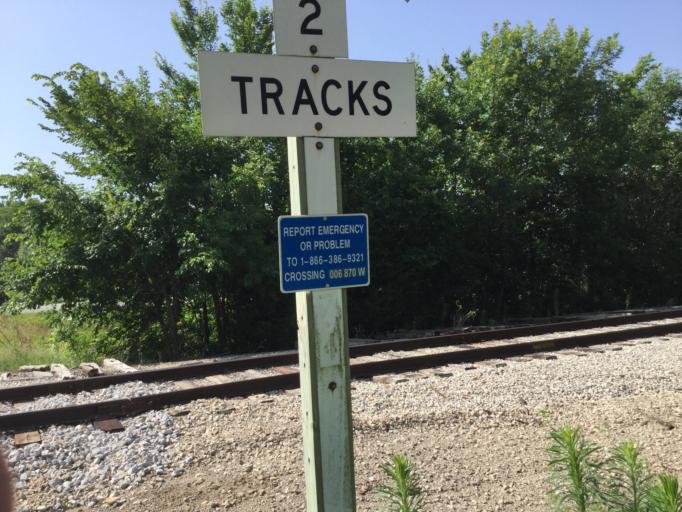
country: US
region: Kansas
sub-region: Montgomery County
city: Independence
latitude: 37.1567
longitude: -95.8059
